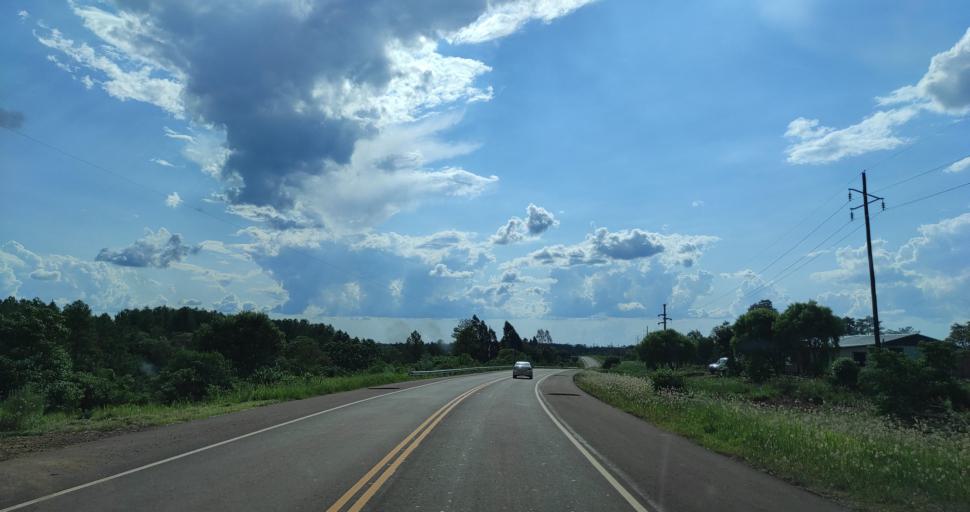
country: AR
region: Misiones
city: Bernardo de Irigoyen
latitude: -26.2994
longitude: -53.8026
